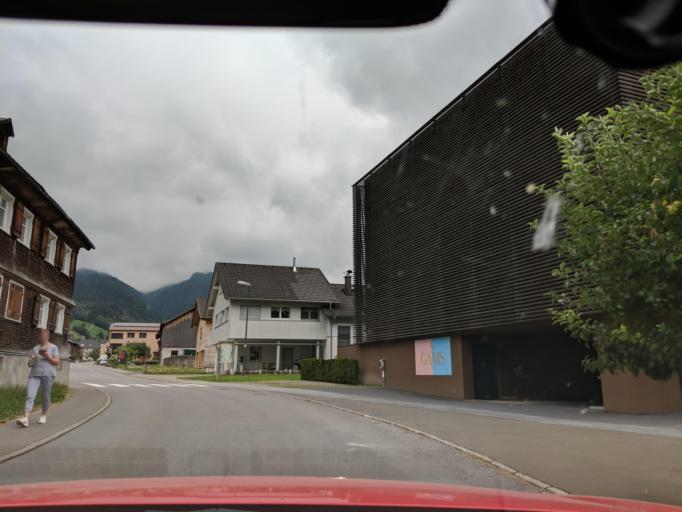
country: AT
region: Vorarlberg
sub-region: Politischer Bezirk Bregenz
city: Bezau
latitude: 47.3857
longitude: 9.9029
